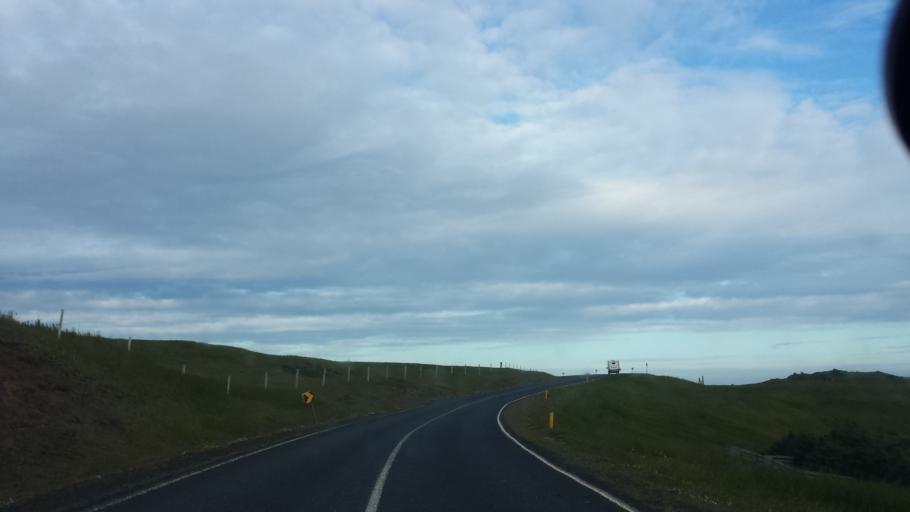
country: IS
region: South
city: Vestmannaeyjar
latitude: 63.4265
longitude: -20.2697
